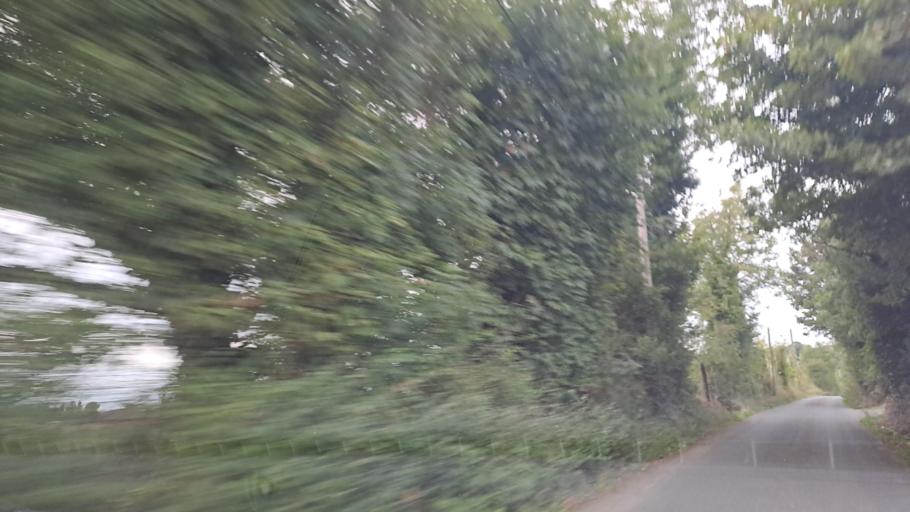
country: IE
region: Ulster
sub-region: An Cabhan
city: Kingscourt
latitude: 53.9863
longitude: -6.8621
